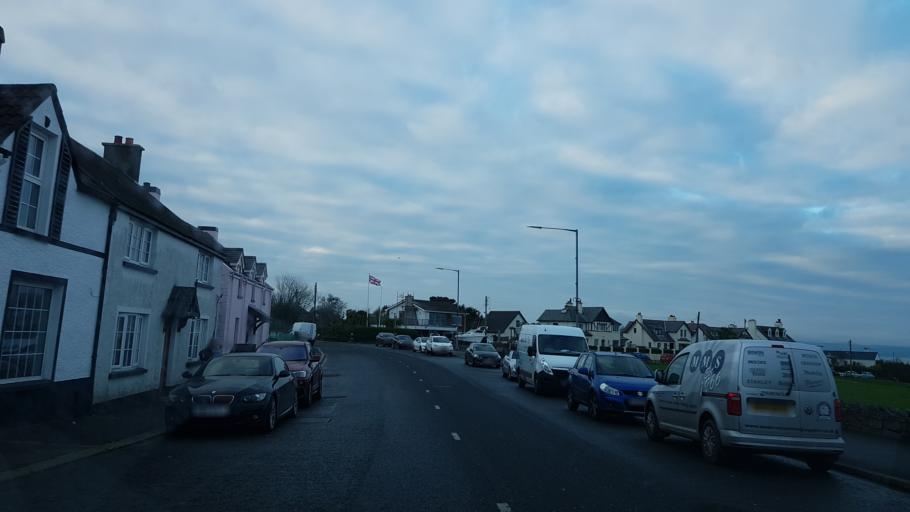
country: GB
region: Northern Ireland
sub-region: North Down District
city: Bangor
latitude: 54.6760
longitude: -5.6198
